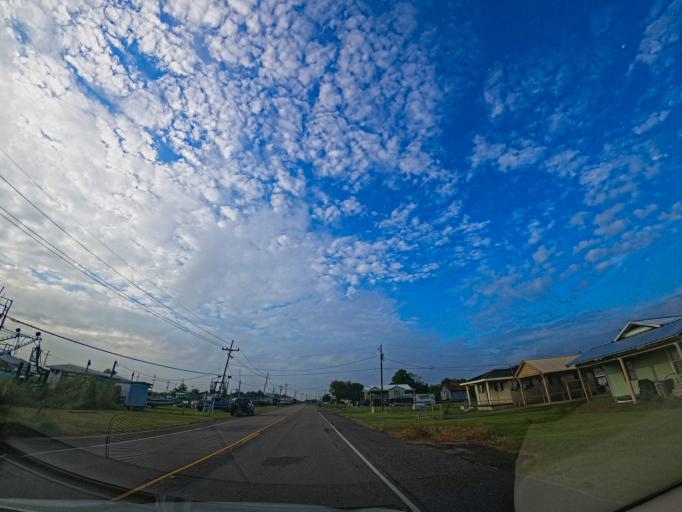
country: US
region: Louisiana
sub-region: Terrebonne Parish
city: Chauvin
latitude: 29.4081
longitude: -90.6077
